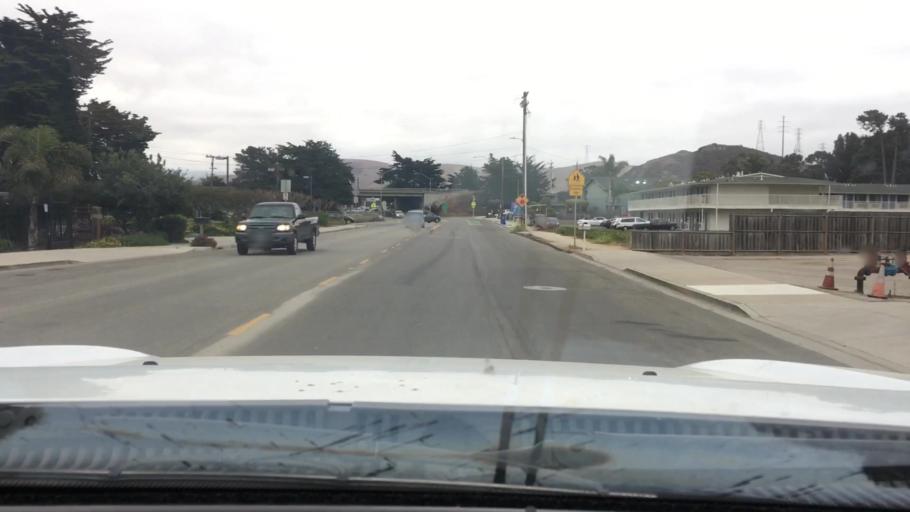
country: US
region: California
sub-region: San Luis Obispo County
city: Morro Bay
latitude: 35.3801
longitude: -120.8583
